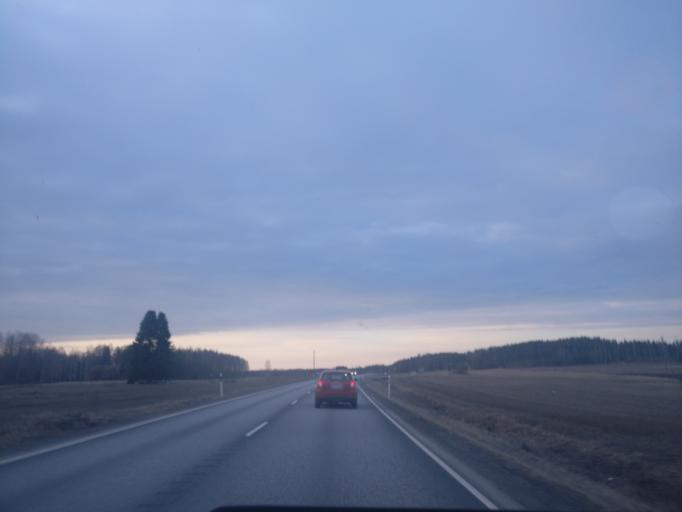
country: FI
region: Paijanne Tavastia
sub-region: Lahti
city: Hartola
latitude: 61.6131
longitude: 26.0072
